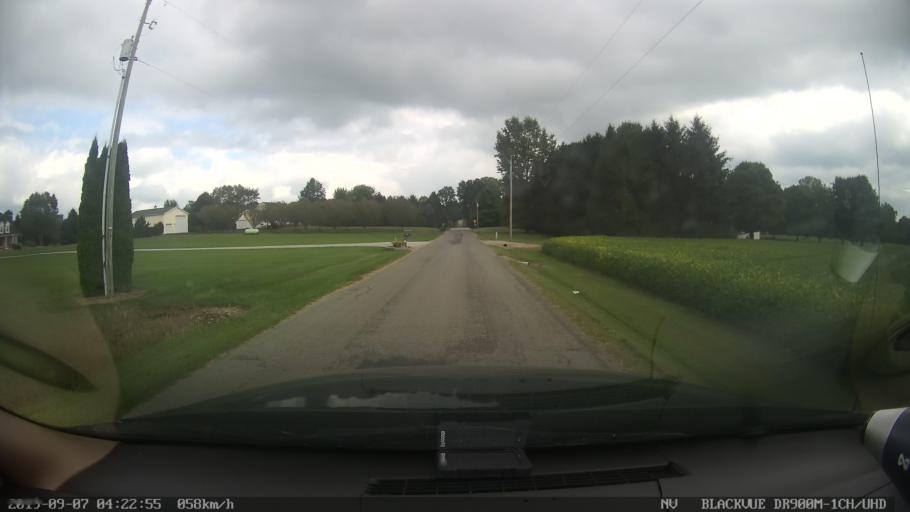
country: US
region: Ohio
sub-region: Knox County
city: Centerburg
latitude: 40.2755
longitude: -82.6712
